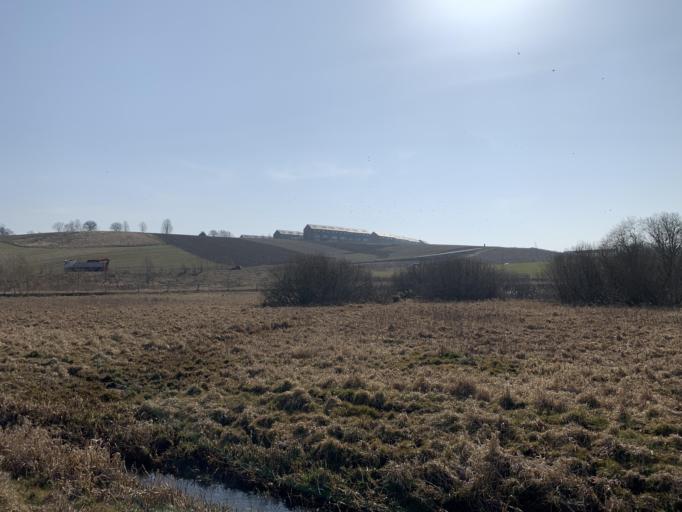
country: DK
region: Capital Region
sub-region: Egedal Kommune
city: Smorumnedre
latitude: 55.7495
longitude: 12.2818
